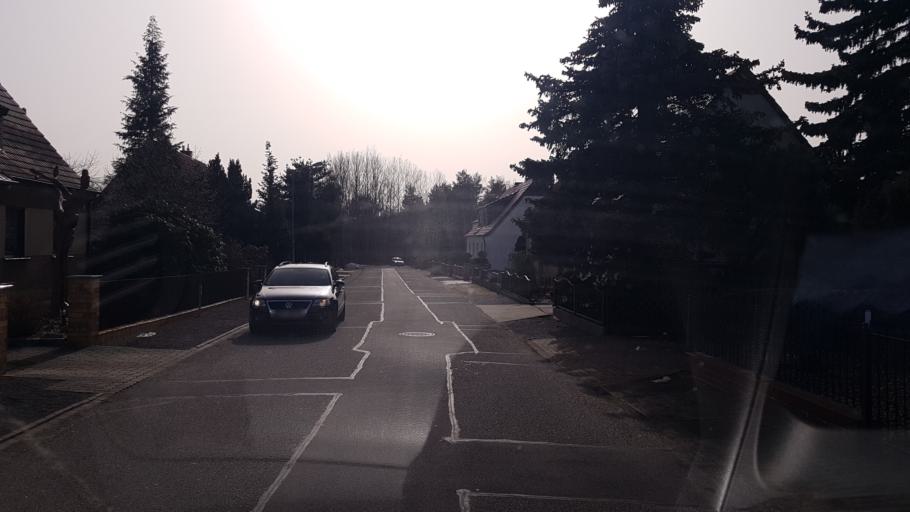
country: DE
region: Brandenburg
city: Lauchhammer
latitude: 51.5034
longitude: 13.7868
